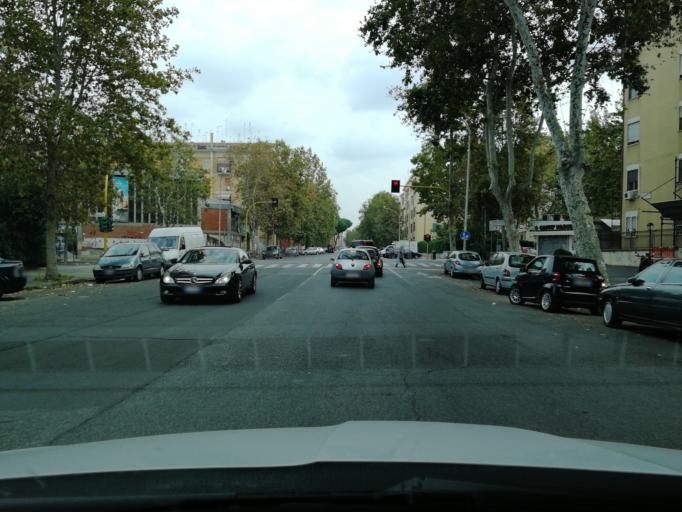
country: IT
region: Latium
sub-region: Citta metropolitana di Roma Capitale
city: Rome
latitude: 41.8590
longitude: 12.5533
